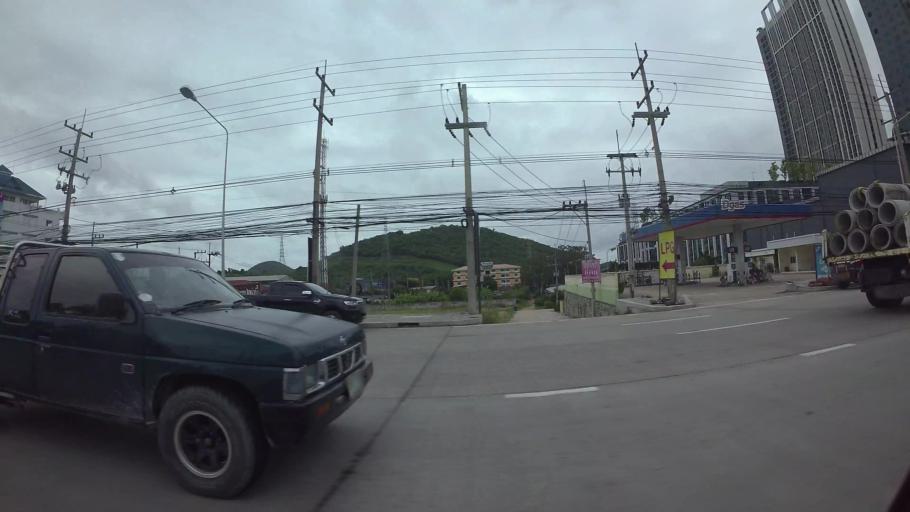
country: TH
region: Chon Buri
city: Si Racha
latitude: 13.1230
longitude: 100.9174
